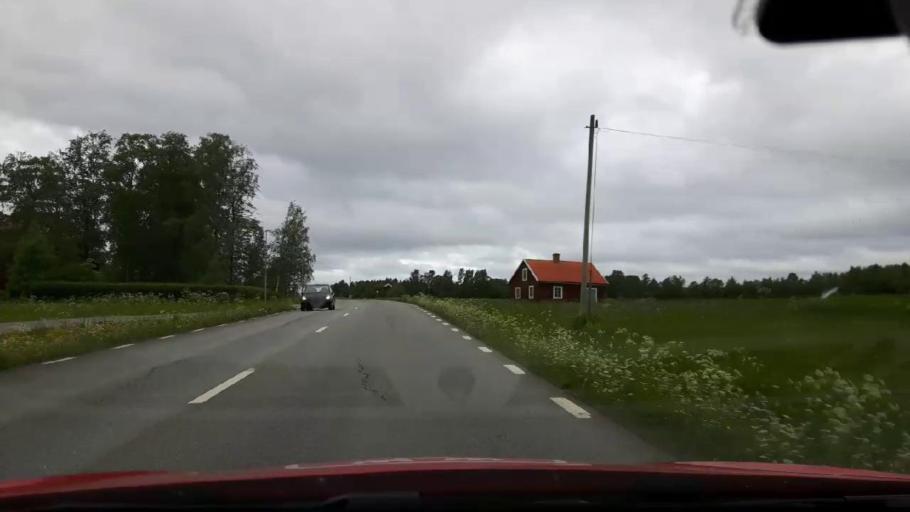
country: SE
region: Jaemtland
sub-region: OEstersunds Kommun
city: Ostersund
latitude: 63.2240
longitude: 14.5983
